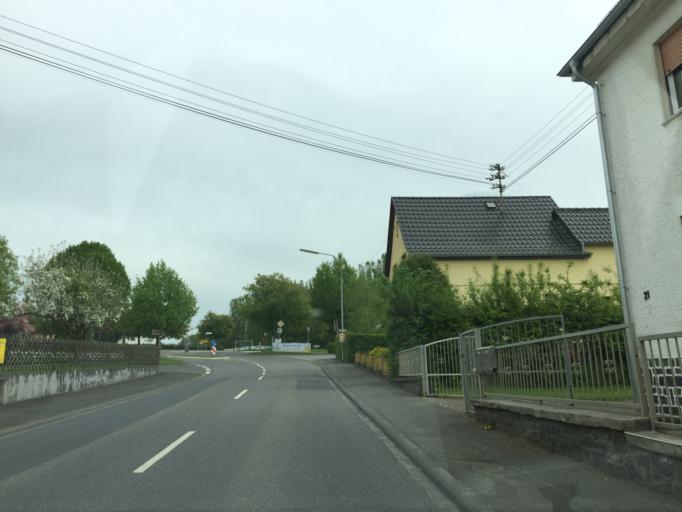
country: DE
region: Rheinland-Pfalz
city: Berod bei Wallmerod
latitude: 50.4804
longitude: 7.9359
